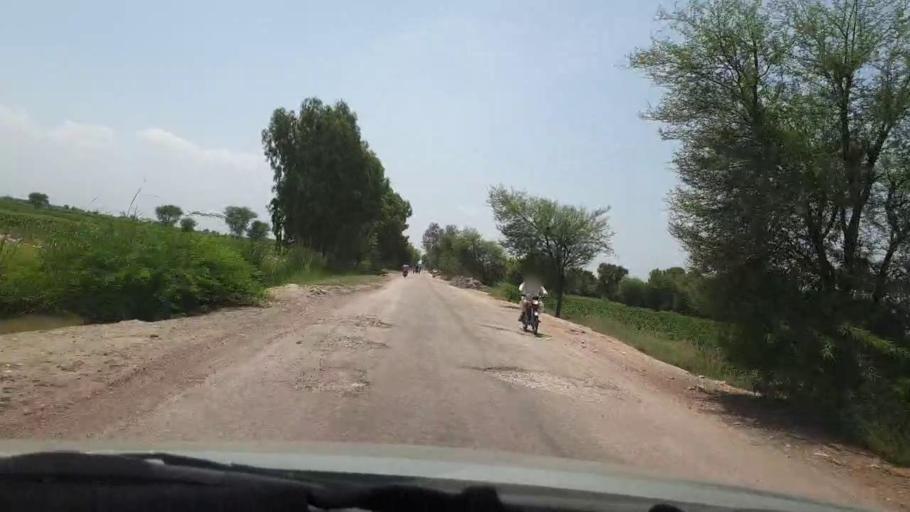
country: PK
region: Sindh
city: Pano Aqil
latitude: 27.6694
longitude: 69.1029
